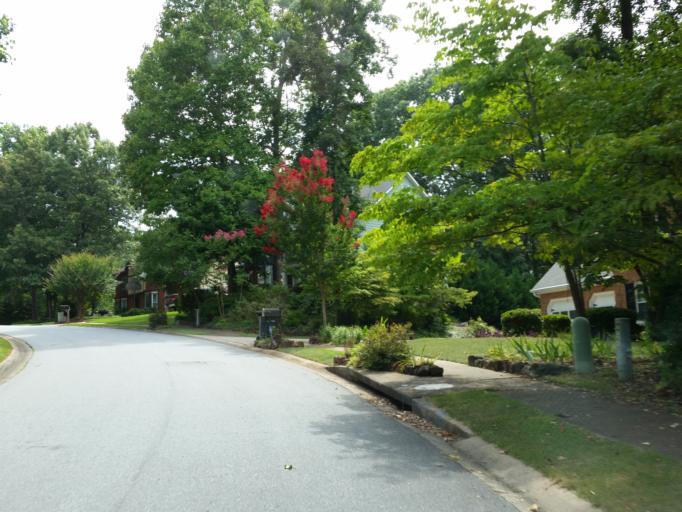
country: US
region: Georgia
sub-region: Cherokee County
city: Woodstock
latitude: 34.0489
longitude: -84.5100
